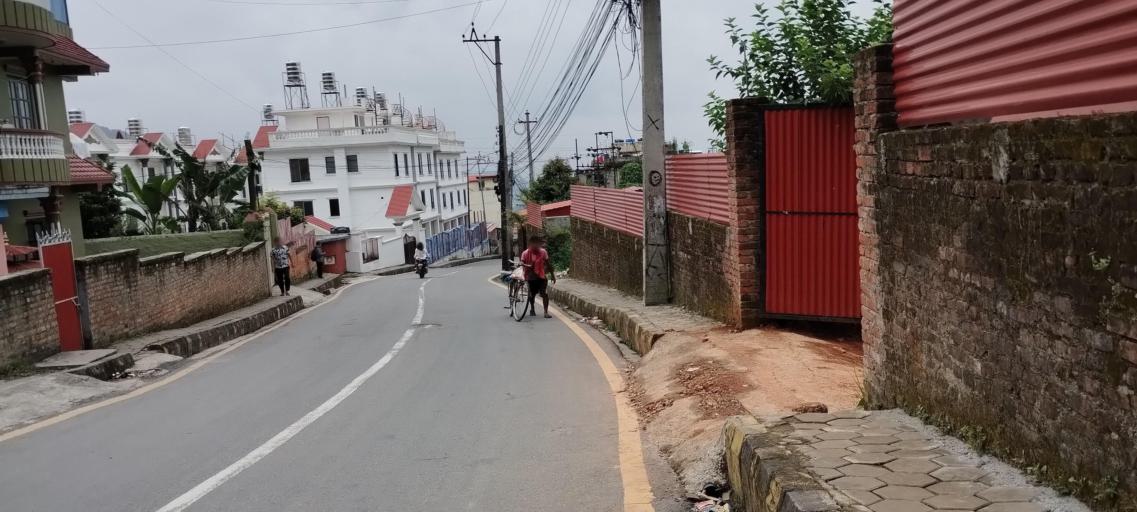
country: NP
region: Central Region
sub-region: Bagmati Zone
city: Kathmandu
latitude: 27.7819
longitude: 85.3638
